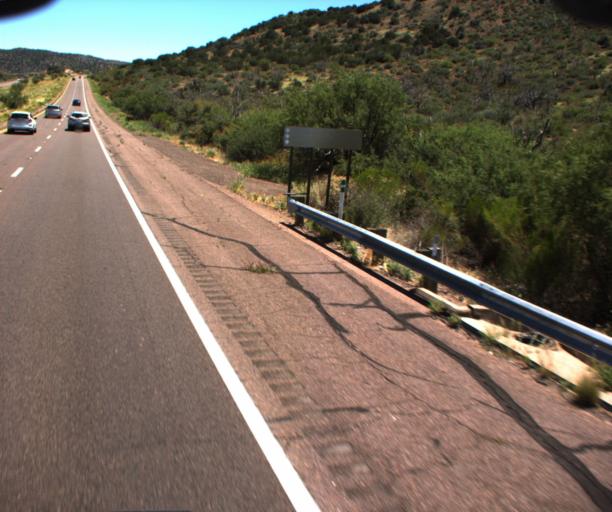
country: US
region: Arizona
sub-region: Gila County
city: Payson
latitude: 34.0299
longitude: -111.3649
